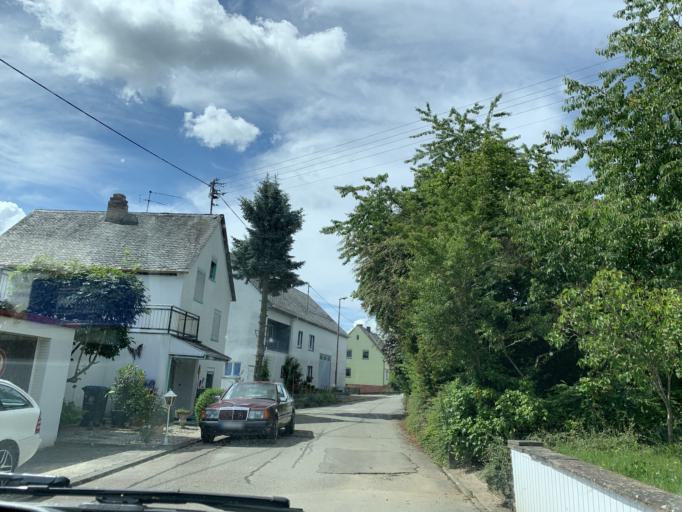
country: DE
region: Rheinland-Pfalz
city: Sosberg
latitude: 50.0779
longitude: 7.3397
